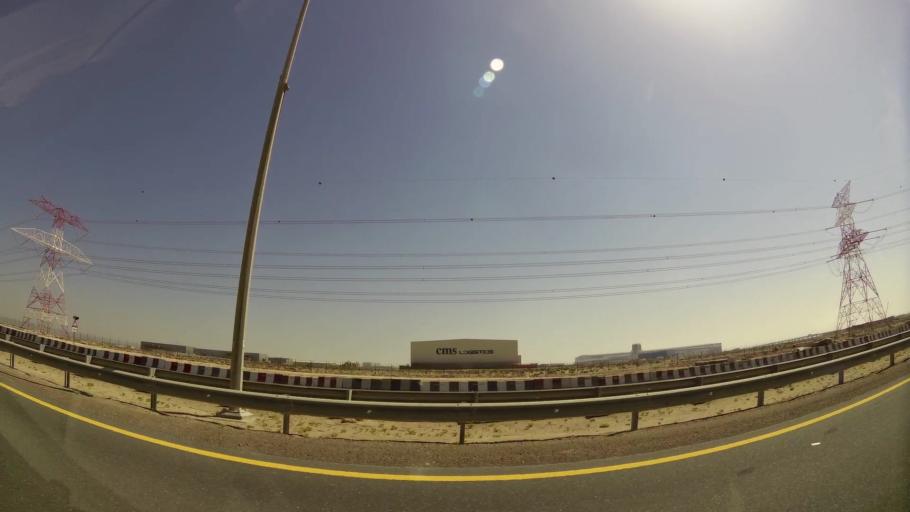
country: AE
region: Dubai
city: Dubai
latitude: 24.9234
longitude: 55.0976
